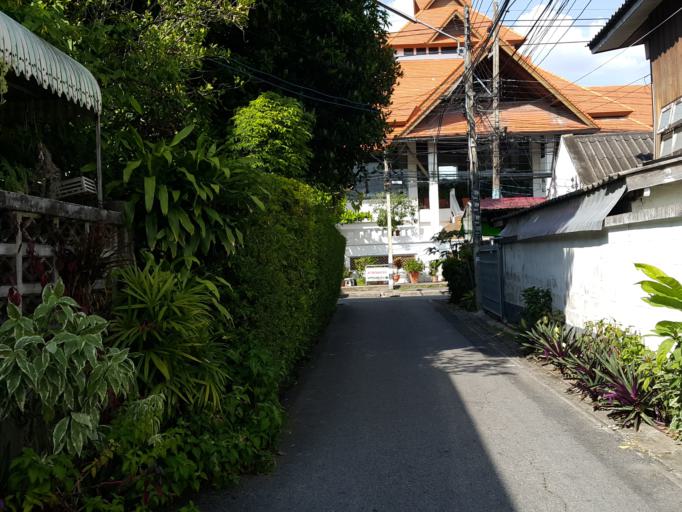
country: TH
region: Chiang Mai
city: Chiang Mai
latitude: 18.7854
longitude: 98.9833
